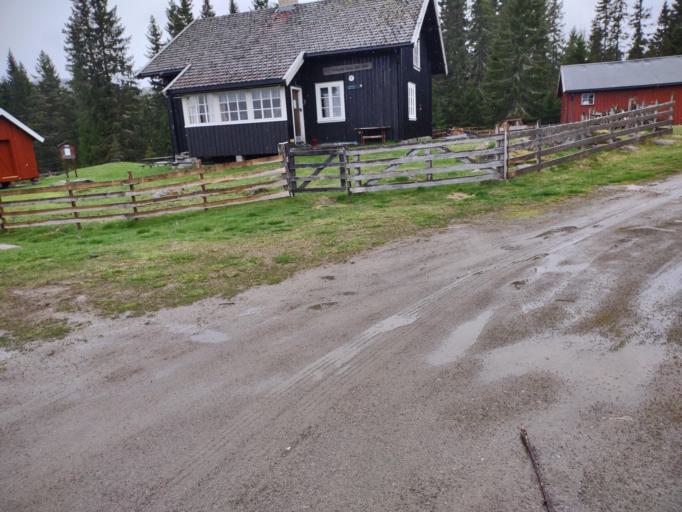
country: NO
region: Oppland
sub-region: Lunner
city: Grua
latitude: 60.3760
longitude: 10.7150
